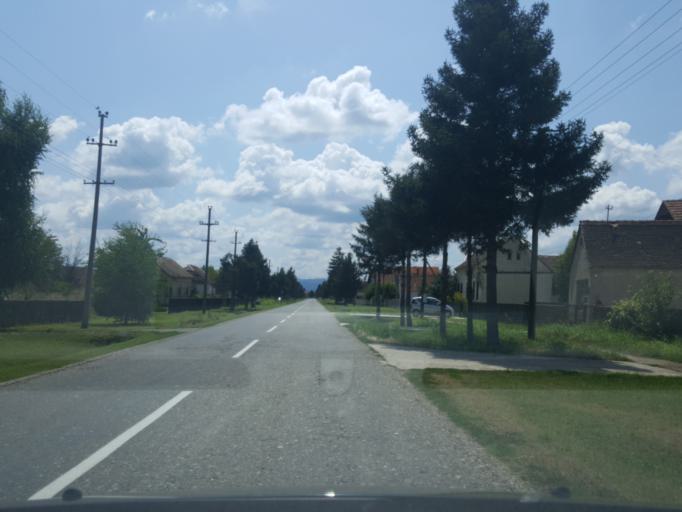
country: RS
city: Zminjak
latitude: 44.7629
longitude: 19.4700
